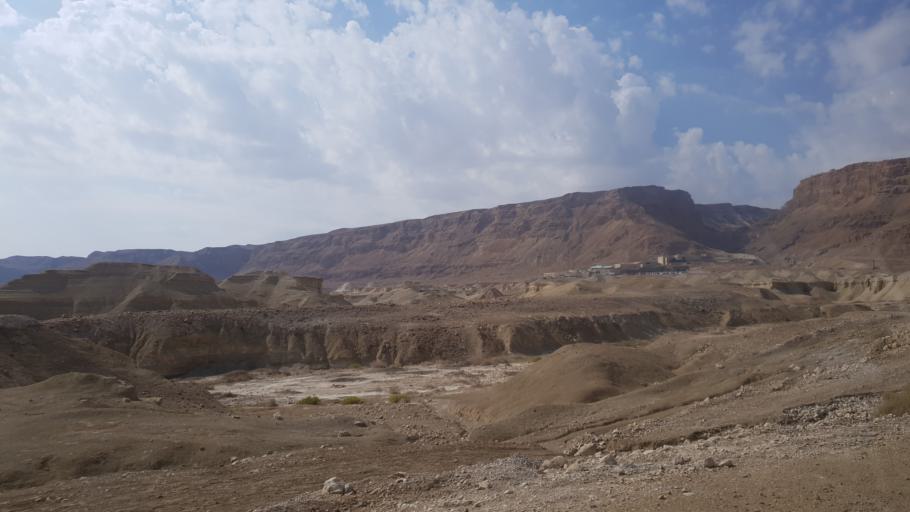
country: IL
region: Southern District
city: `En Boqeq
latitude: 31.3170
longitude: 35.3781
